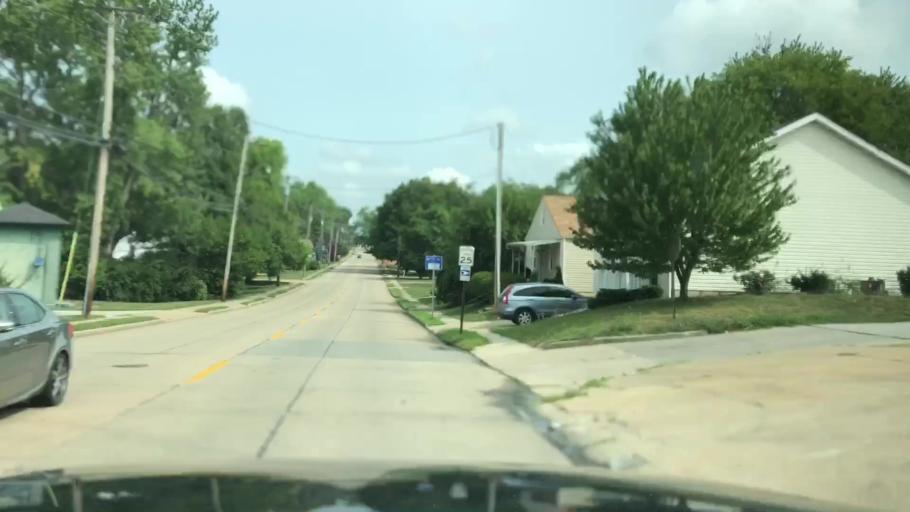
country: US
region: Missouri
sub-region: Saint Charles County
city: Wentzville
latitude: 38.8130
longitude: -90.8505
